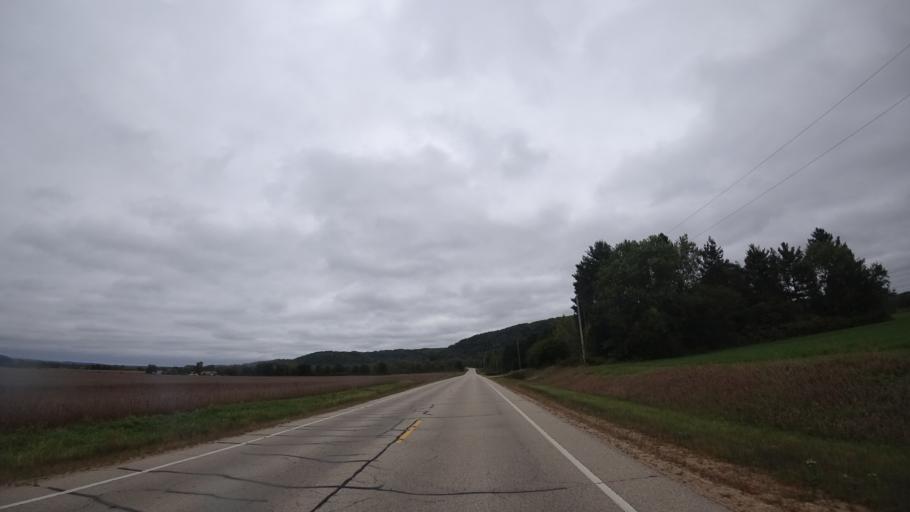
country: US
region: Wisconsin
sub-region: Grant County
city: Boscobel
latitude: 43.2053
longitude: -90.6318
